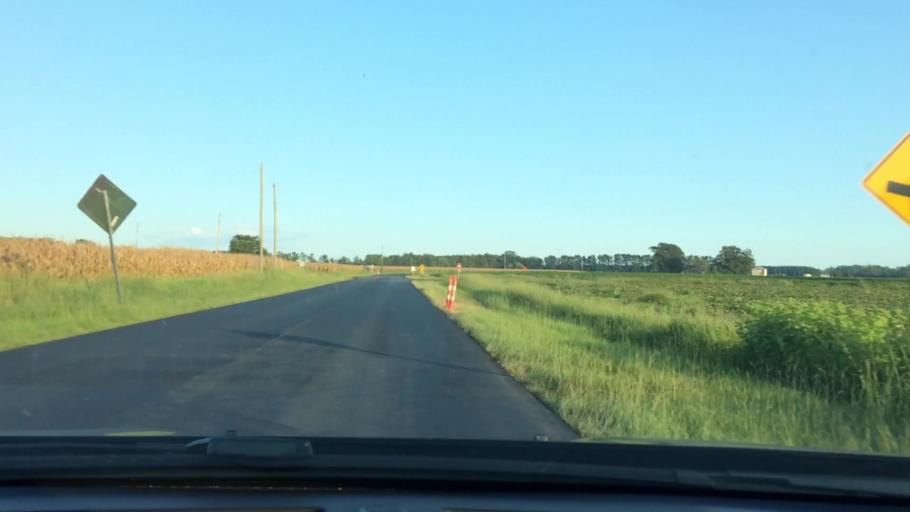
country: US
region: North Carolina
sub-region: Pitt County
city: Ayden
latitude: 35.4439
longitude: -77.4559
